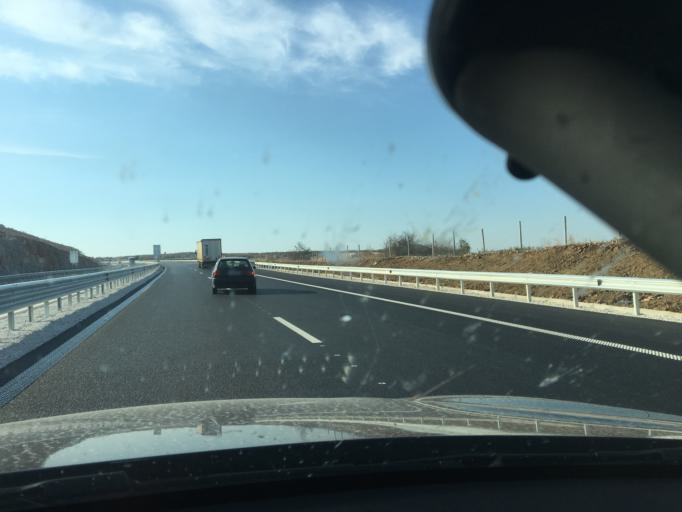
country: BG
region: Lovech
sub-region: Obshtina Yablanitsa
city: Yablanitsa
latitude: 43.0531
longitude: 24.2068
